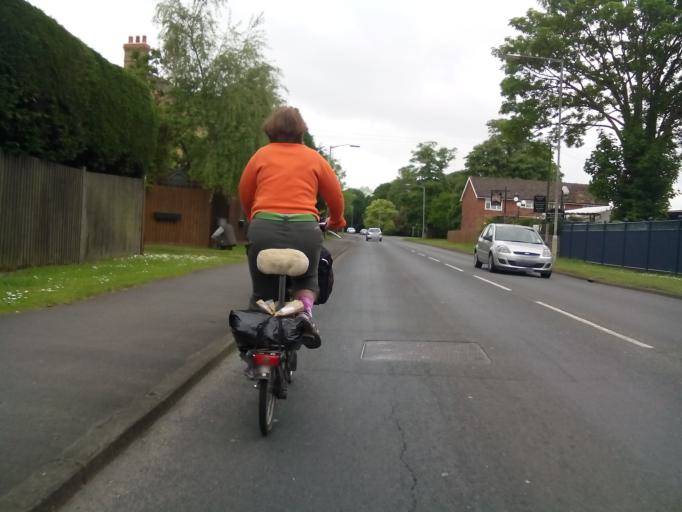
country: GB
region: England
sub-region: Cambridgeshire
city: Godmanchester
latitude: 52.3378
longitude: -0.1590
